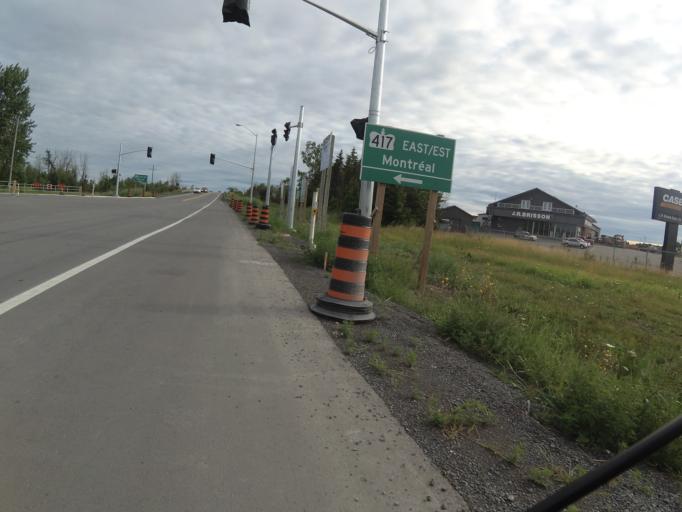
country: CA
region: Ontario
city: Bourget
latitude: 45.3329
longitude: -75.3499
